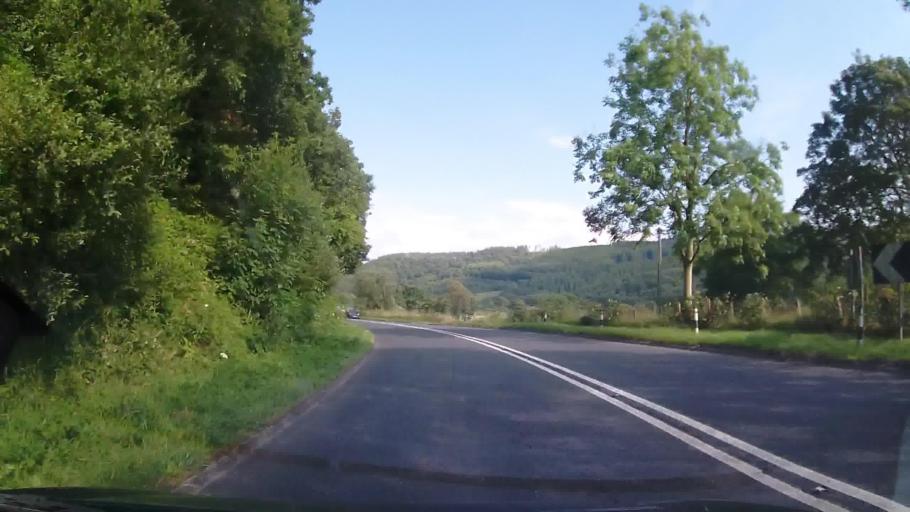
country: GB
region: Wales
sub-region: Gwynedd
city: Penrhyndeudraeth
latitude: 52.9408
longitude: -4.0289
